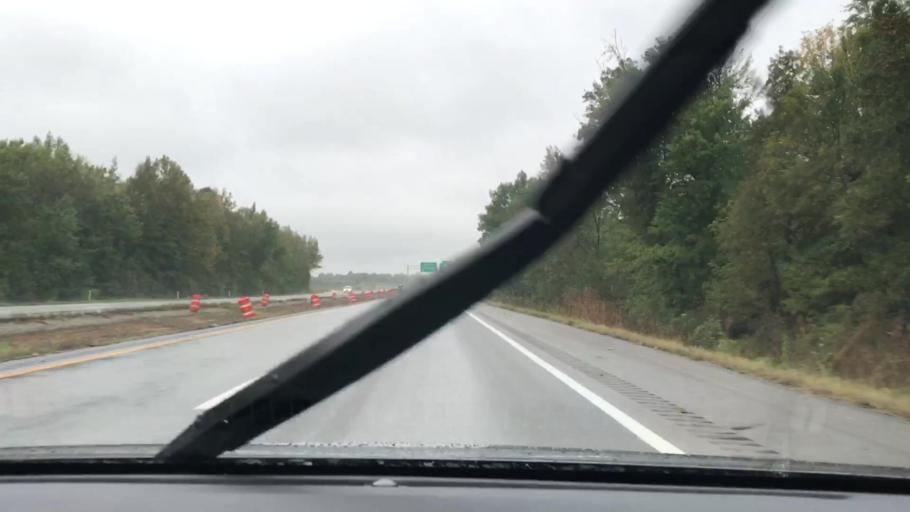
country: US
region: Kentucky
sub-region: Hopkins County
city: Nortonville
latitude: 37.1572
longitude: -87.4605
